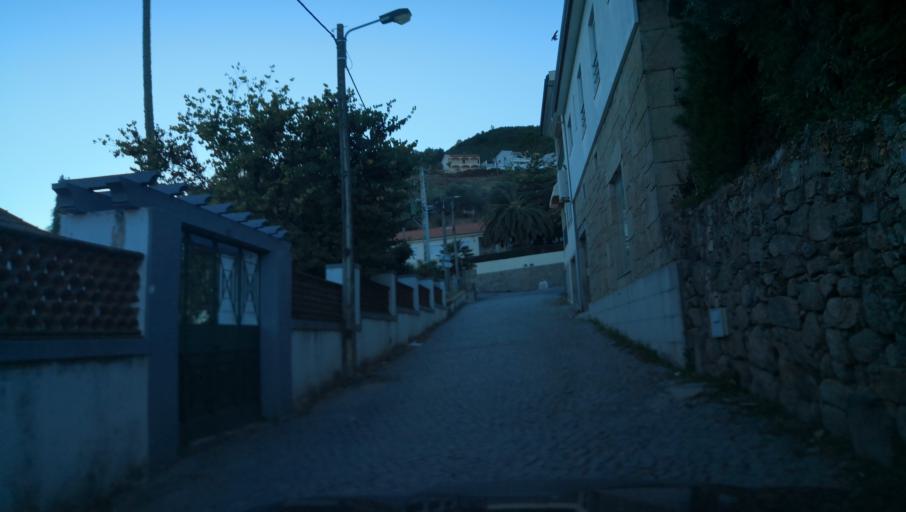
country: PT
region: Vila Real
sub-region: Vila Real
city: Vila Real
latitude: 41.2560
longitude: -7.7704
